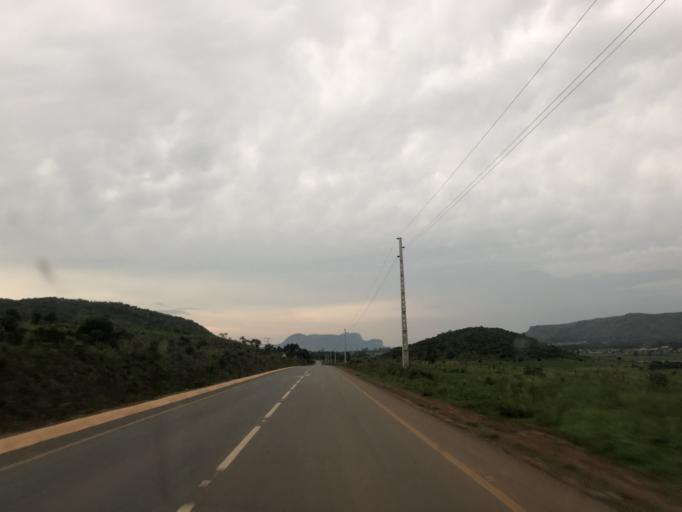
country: AO
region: Cuanza Sul
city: Uacu Cungo
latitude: -11.3266
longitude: 15.0918
